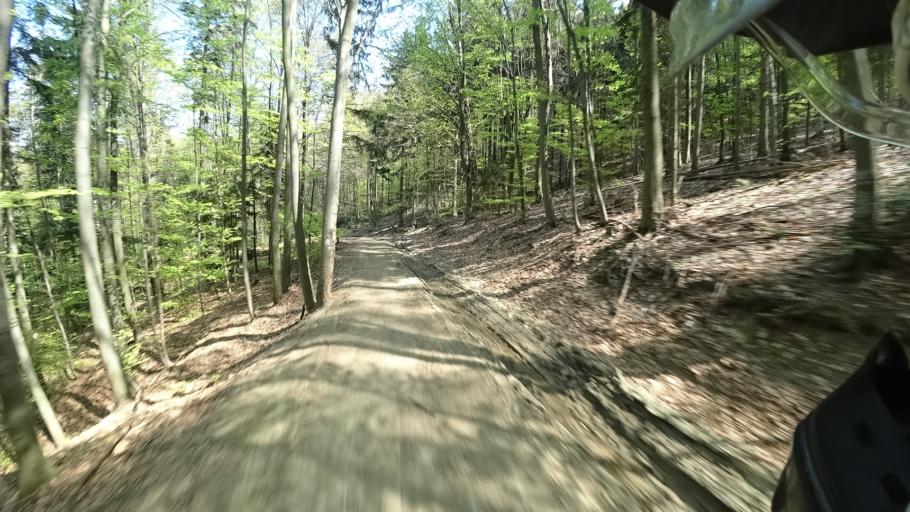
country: HR
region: Zagrebacka
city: Jablanovec
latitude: 45.8999
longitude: 15.9168
